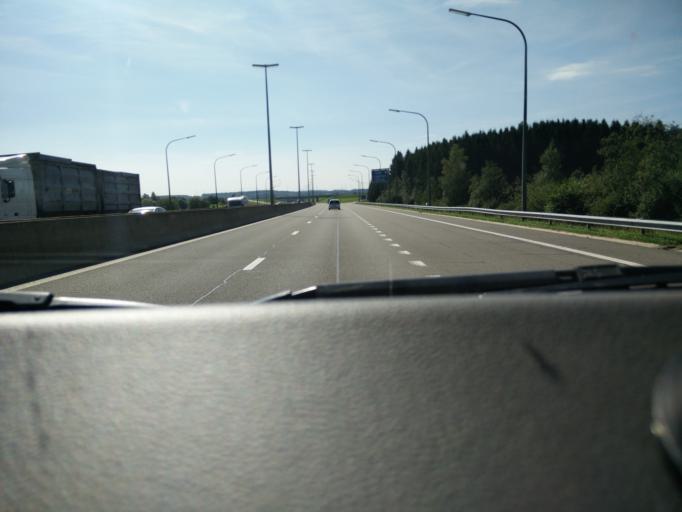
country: BE
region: Wallonia
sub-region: Province du Luxembourg
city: Leglise
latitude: 49.8138
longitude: 5.5157
